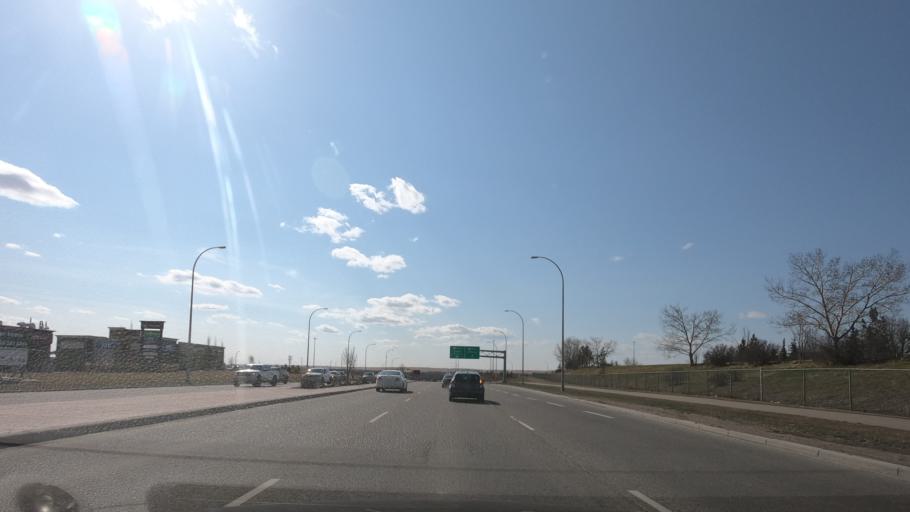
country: CA
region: Alberta
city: Airdrie
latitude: 51.2709
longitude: -113.9956
